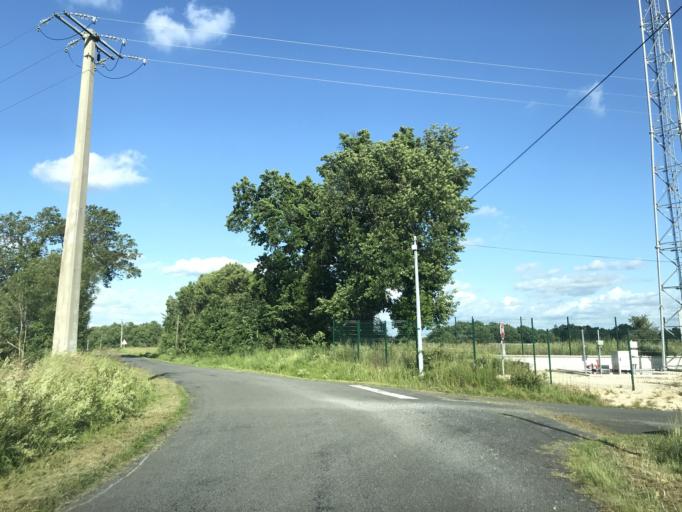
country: FR
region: Poitou-Charentes
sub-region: Departement de la Charente
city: Chalais
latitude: 45.2735
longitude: -0.0224
